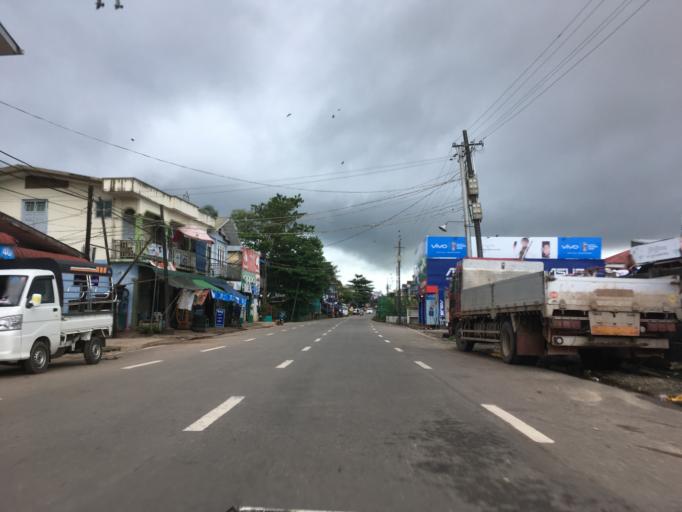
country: MM
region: Mon
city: Mawlamyine
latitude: 16.4649
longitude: 97.6239
